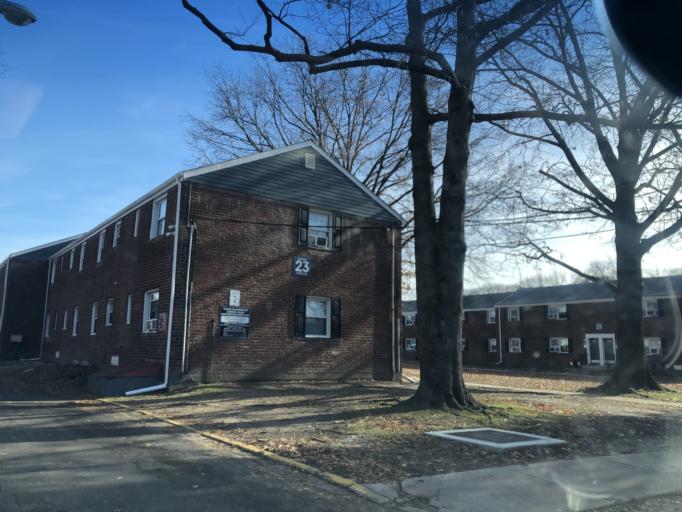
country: US
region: New Jersey
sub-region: Bergen County
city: Elmwood Park
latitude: 40.9163
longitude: -74.1254
